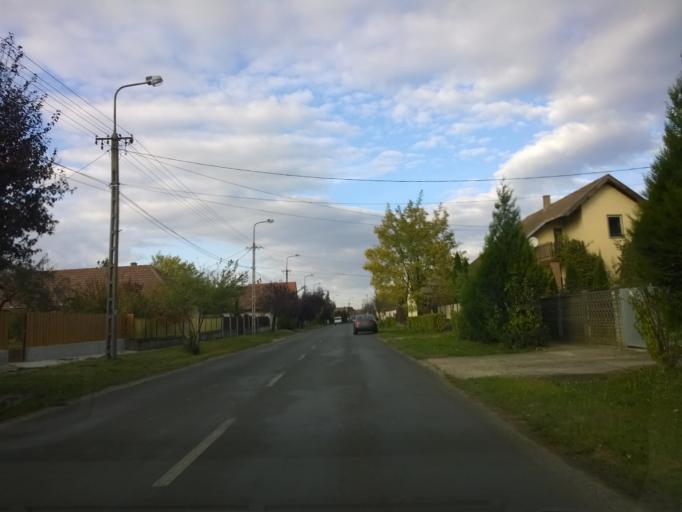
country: HU
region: Pest
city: Szigetujfalu
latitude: 47.2342
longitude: 18.9593
